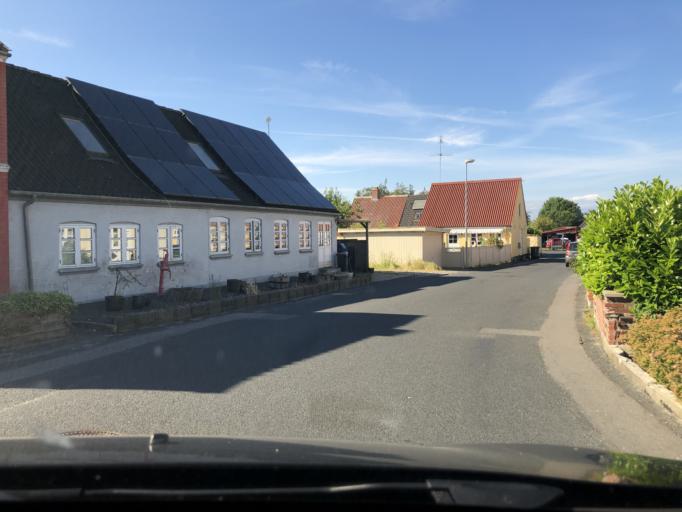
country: DK
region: South Denmark
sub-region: AEro Kommune
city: Marstal
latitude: 54.8720
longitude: 10.4894
